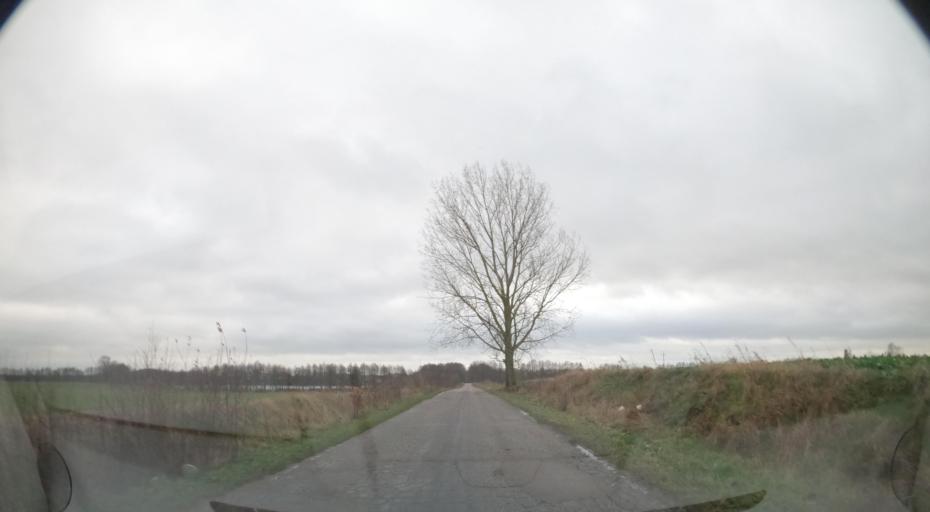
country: PL
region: Greater Poland Voivodeship
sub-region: Powiat pilski
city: Wysoka
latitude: 53.2603
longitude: 17.1155
